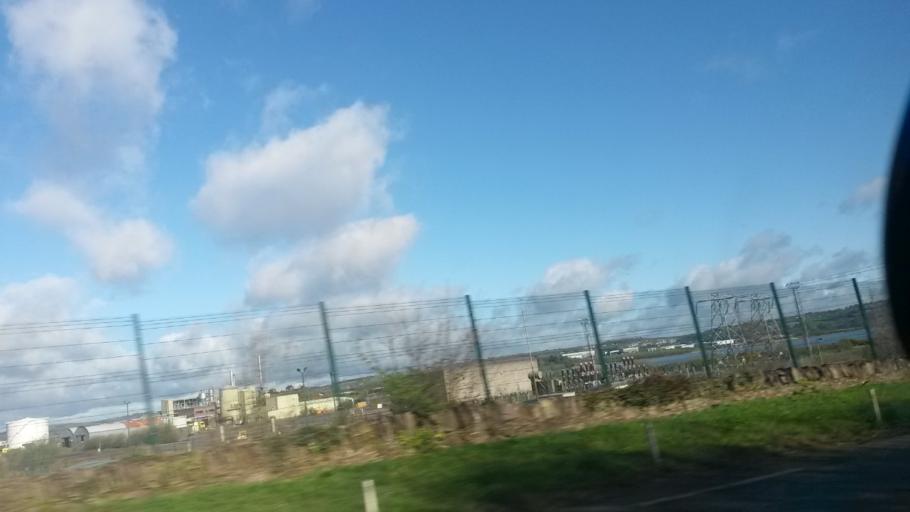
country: IE
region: Munster
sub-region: County Cork
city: Passage West
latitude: 51.8777
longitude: -8.3232
